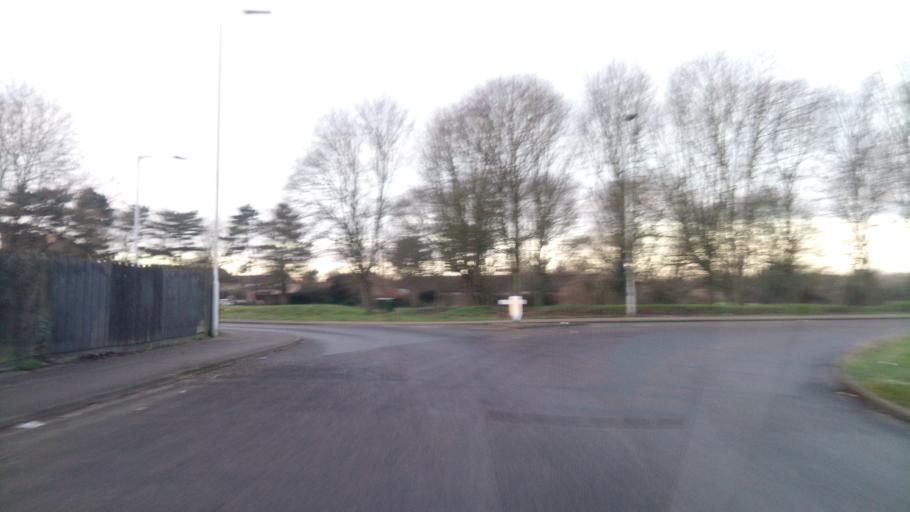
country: GB
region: England
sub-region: Peterborough
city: Peterborough
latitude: 52.5834
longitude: -0.2696
